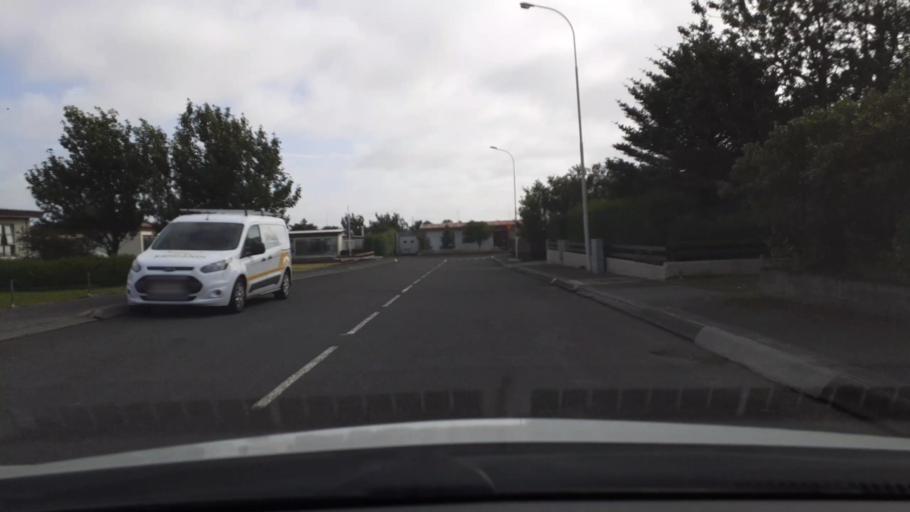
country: IS
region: South
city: THorlakshoefn
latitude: 63.8538
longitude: -21.3912
